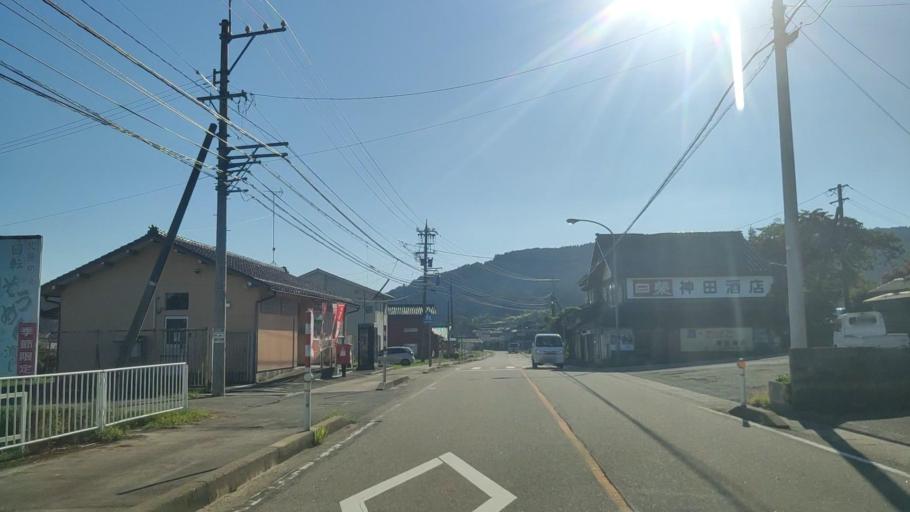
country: JP
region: Ishikawa
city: Nanao
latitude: 37.1477
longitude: 136.8751
